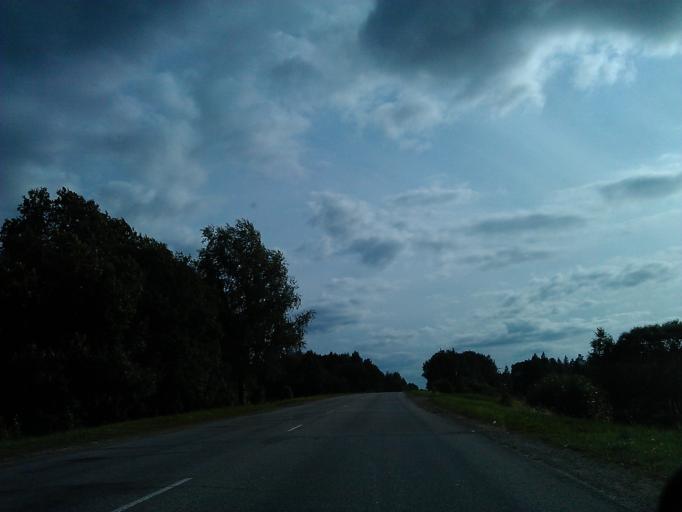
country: LV
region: Cesu Rajons
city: Cesis
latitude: 57.2867
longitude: 25.2979
